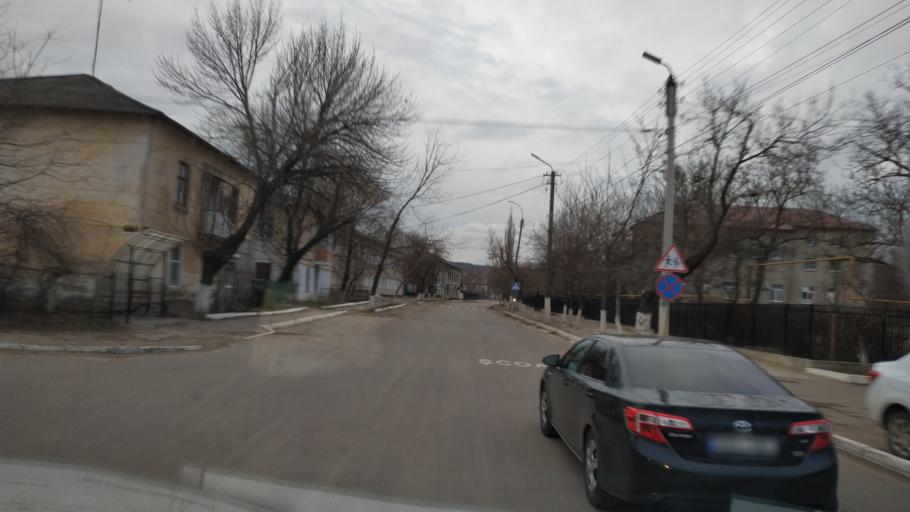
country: MD
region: Causeni
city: Causeni
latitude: 46.6392
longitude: 29.4060
